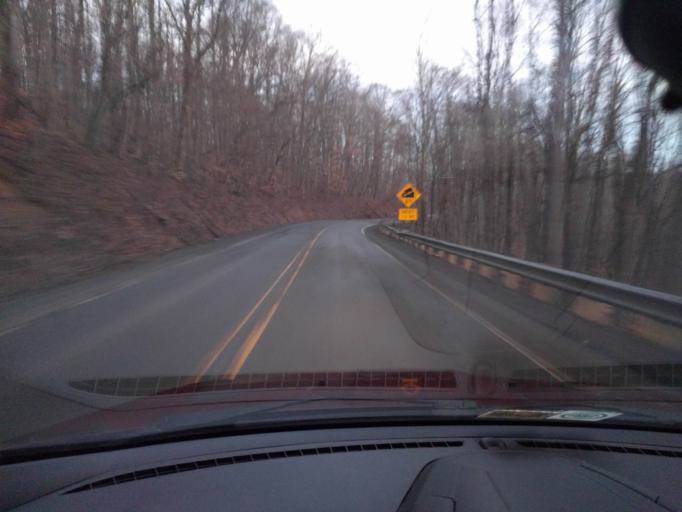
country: US
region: West Virginia
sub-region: Greenbrier County
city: Rainelle
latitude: 37.9874
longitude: -80.8546
